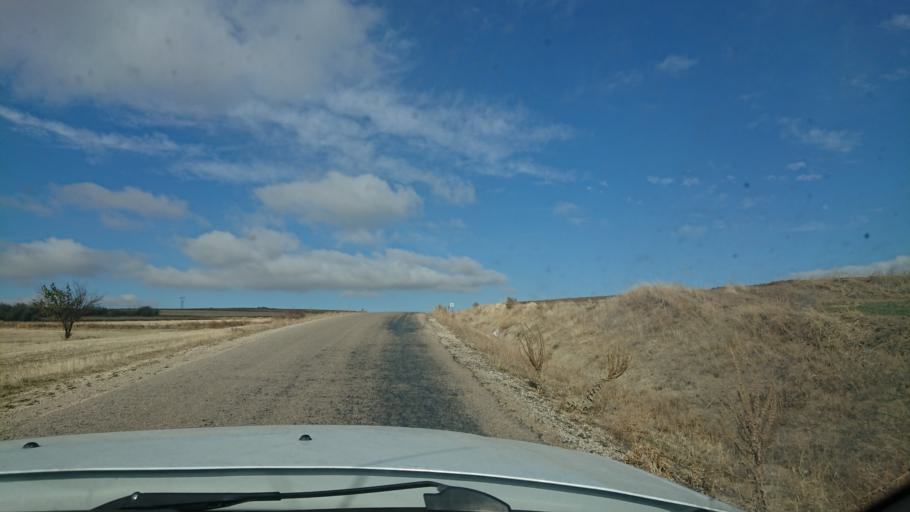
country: TR
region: Aksaray
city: Agacoren
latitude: 38.8344
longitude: 33.9554
